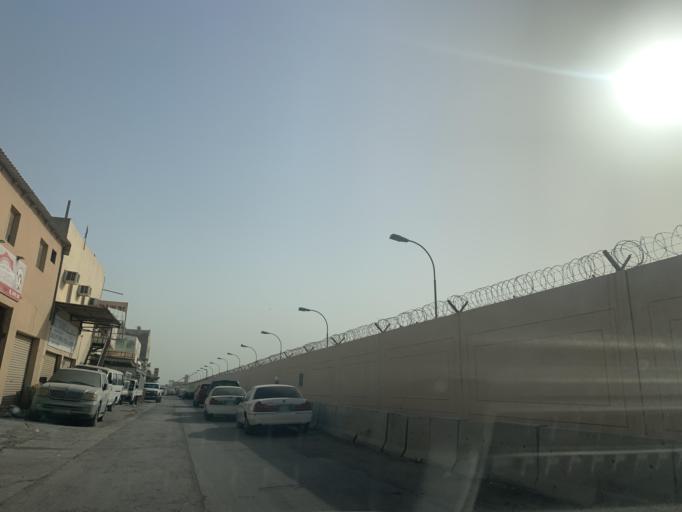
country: BH
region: Central Governorate
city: Madinat Hamad
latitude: 26.1490
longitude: 50.4852
